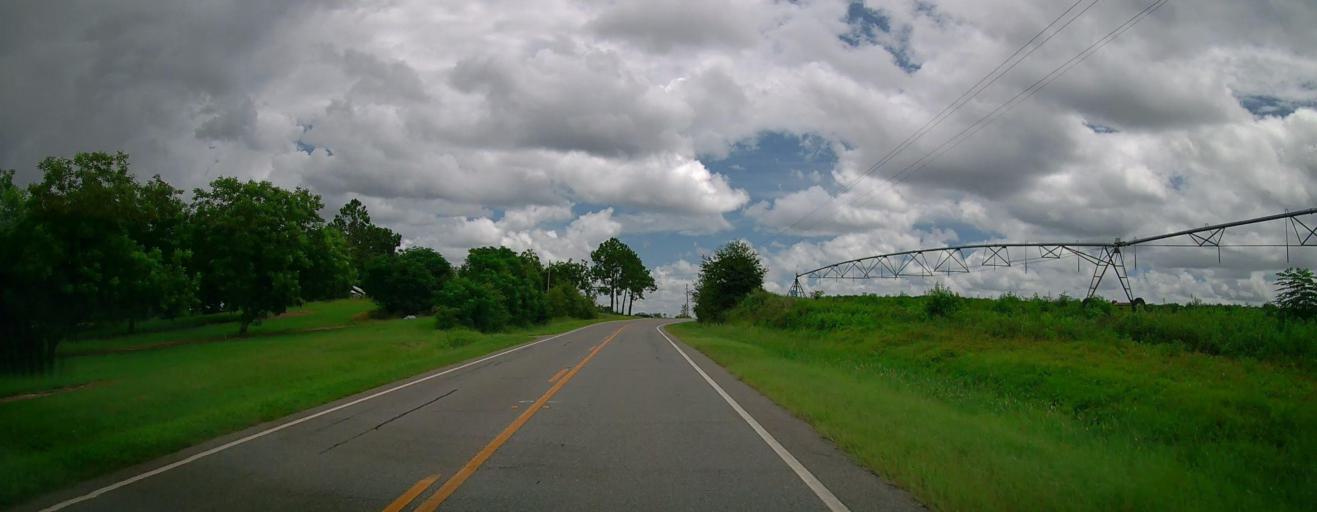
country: US
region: Georgia
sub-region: Wilcox County
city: Rochelle
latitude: 32.0221
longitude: -83.5603
